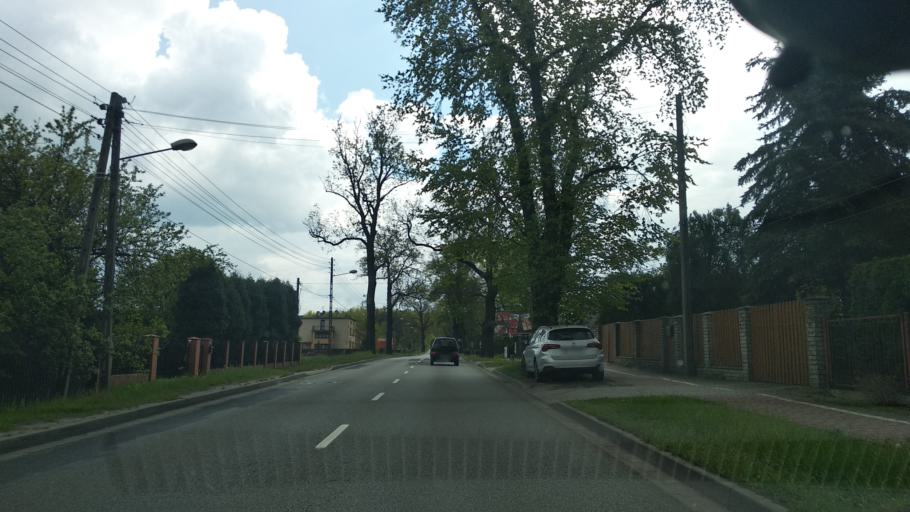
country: PL
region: Silesian Voivodeship
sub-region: Powiat mikolowski
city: Mikolow
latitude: 50.2251
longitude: 18.9247
